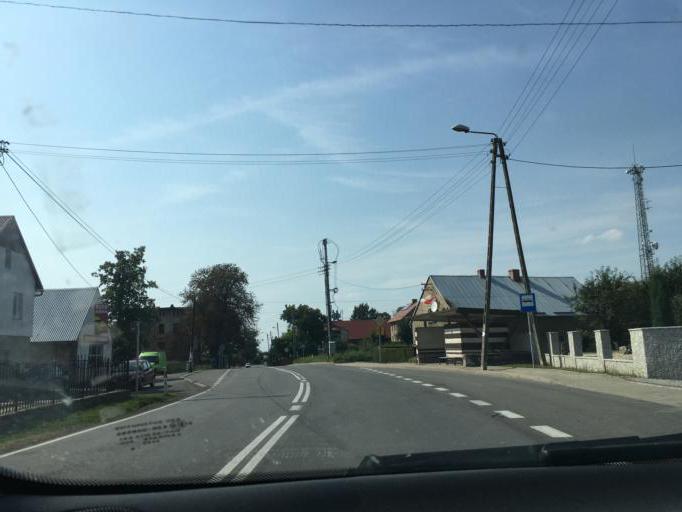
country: PL
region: Opole Voivodeship
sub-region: Powiat nyski
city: Nysa
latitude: 50.4248
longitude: 17.4338
